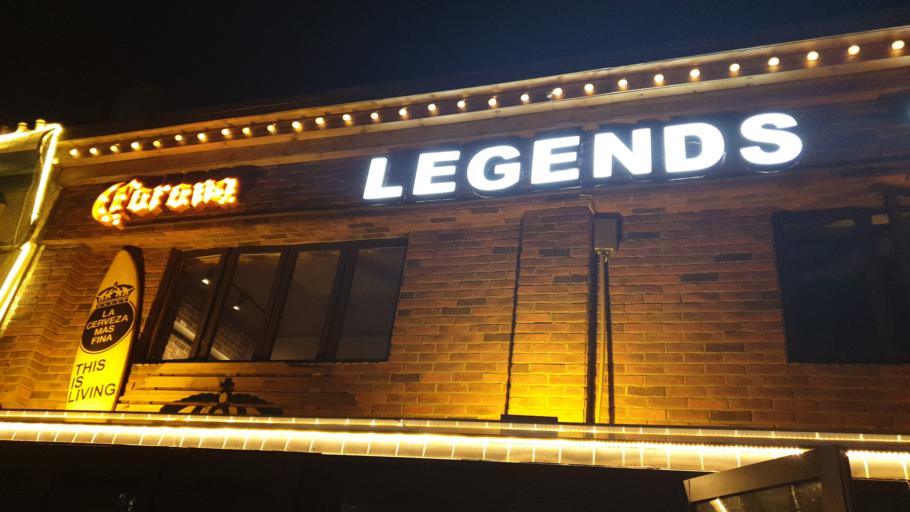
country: CN
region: Shanghai Shi
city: Changning
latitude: 31.1932
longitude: 121.3823
